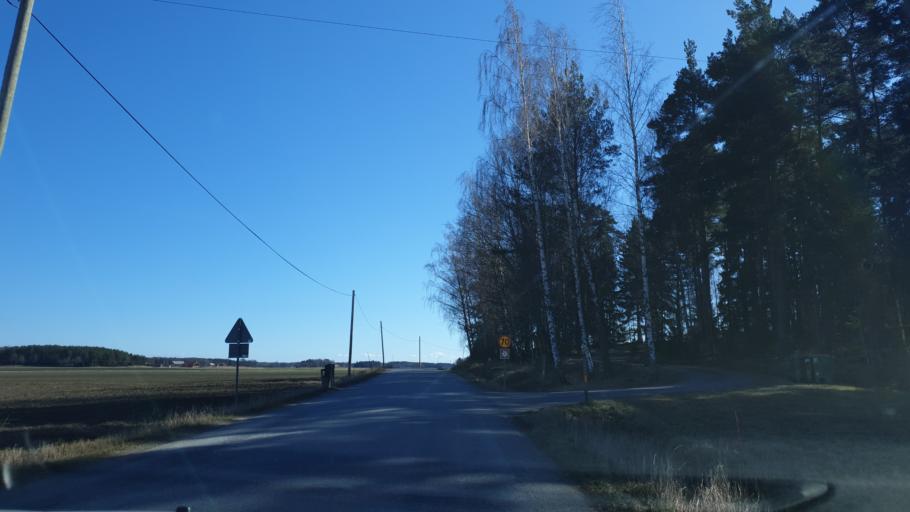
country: SE
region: Uppsala
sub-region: Enkopings Kommun
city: Grillby
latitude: 59.5802
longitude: 17.2853
